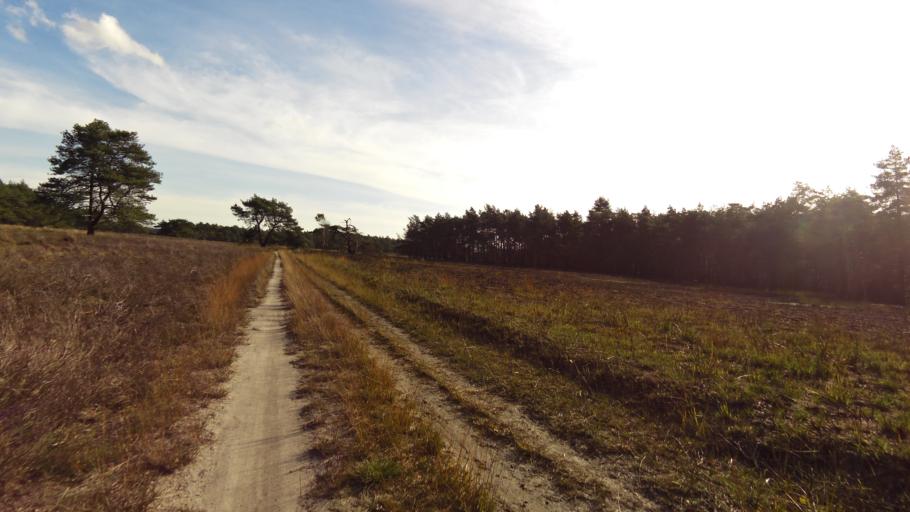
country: NL
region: Gelderland
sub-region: Gemeente Epe
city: Emst
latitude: 52.3378
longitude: 5.8952
